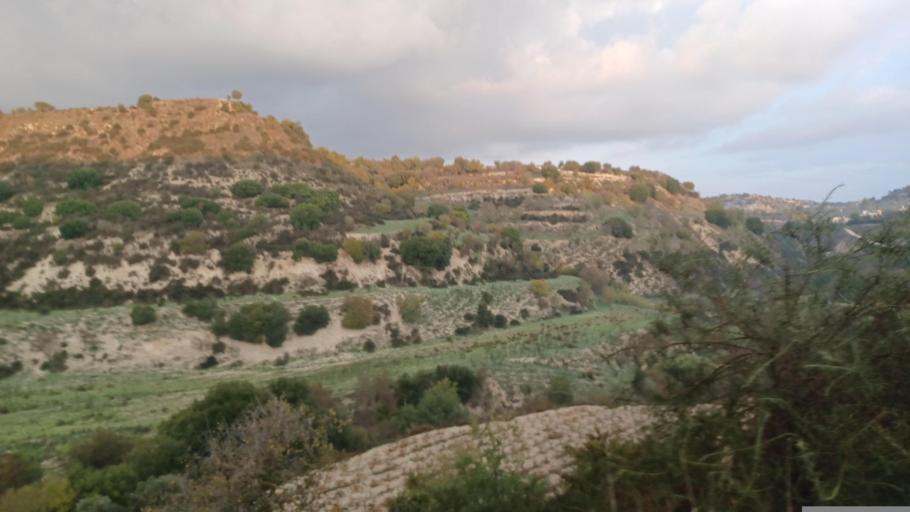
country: CY
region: Pafos
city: Mesogi
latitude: 34.8444
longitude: 32.5199
